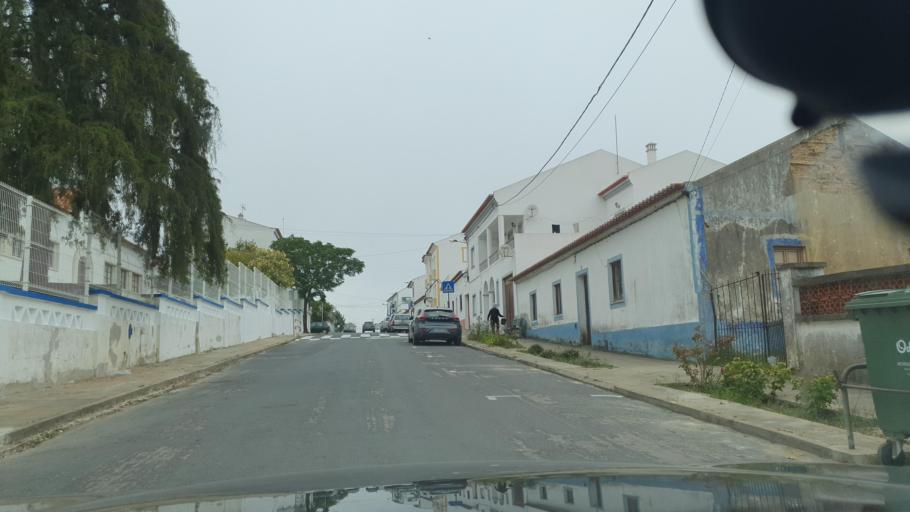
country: PT
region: Beja
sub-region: Odemira
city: Sao Teotonio
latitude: 37.5107
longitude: -8.7036
